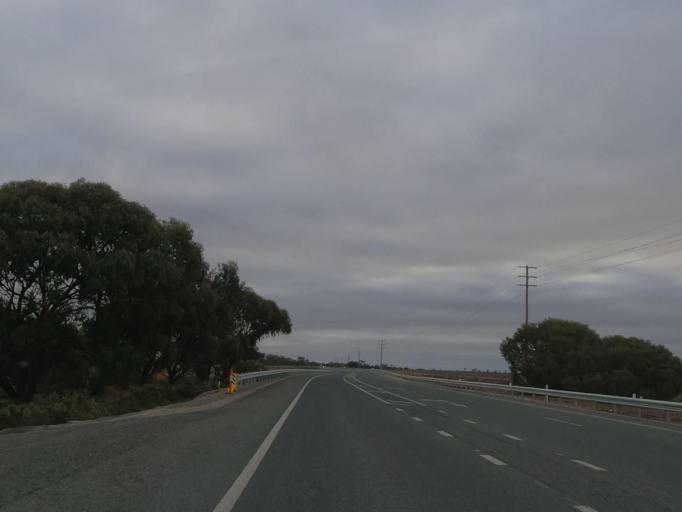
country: AU
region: Victoria
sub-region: Swan Hill
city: Swan Hill
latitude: -35.5448
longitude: 143.7589
